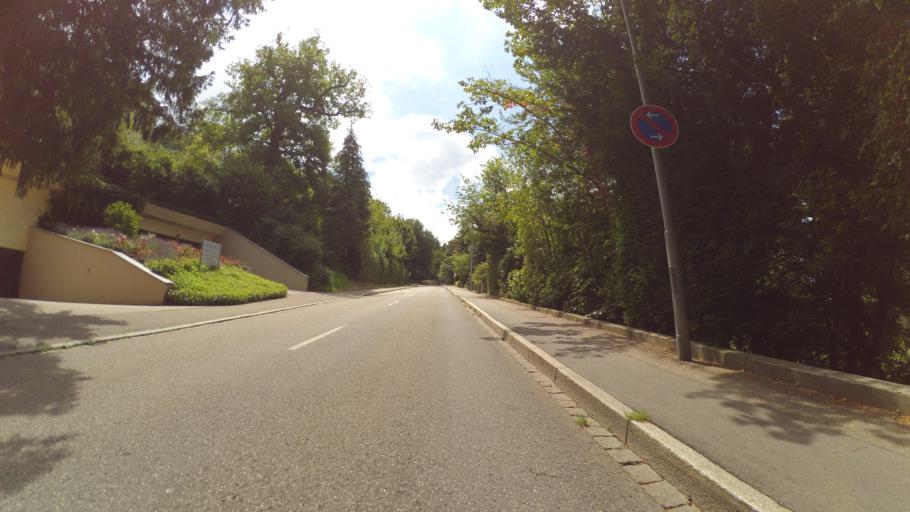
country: DE
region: Baden-Wuerttemberg
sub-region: Freiburg Region
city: Badenweiler
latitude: 47.7986
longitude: 7.6702
